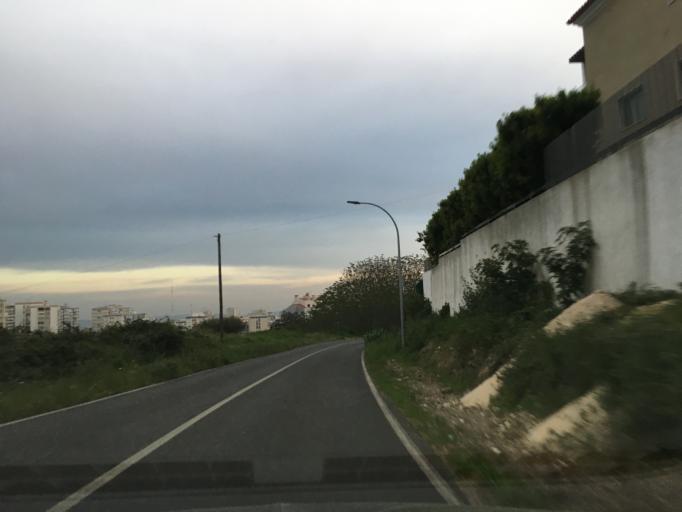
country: PT
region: Lisbon
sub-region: Oeiras
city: Carnaxide
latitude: 38.7309
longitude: -9.2383
